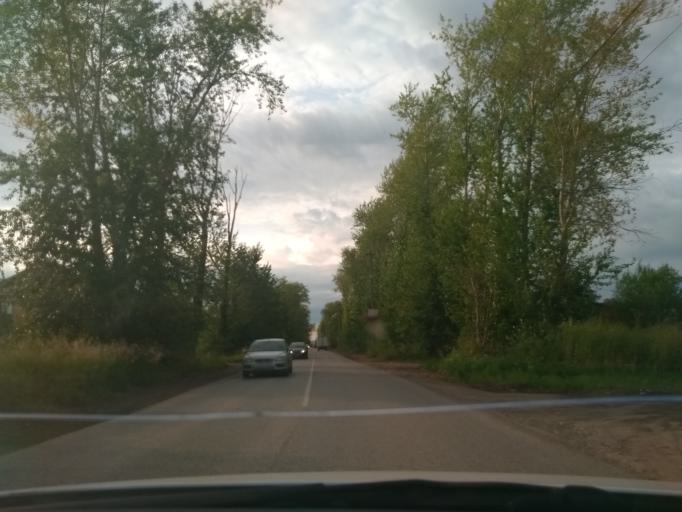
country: RU
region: Perm
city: Perm
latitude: 57.9972
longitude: 56.3360
